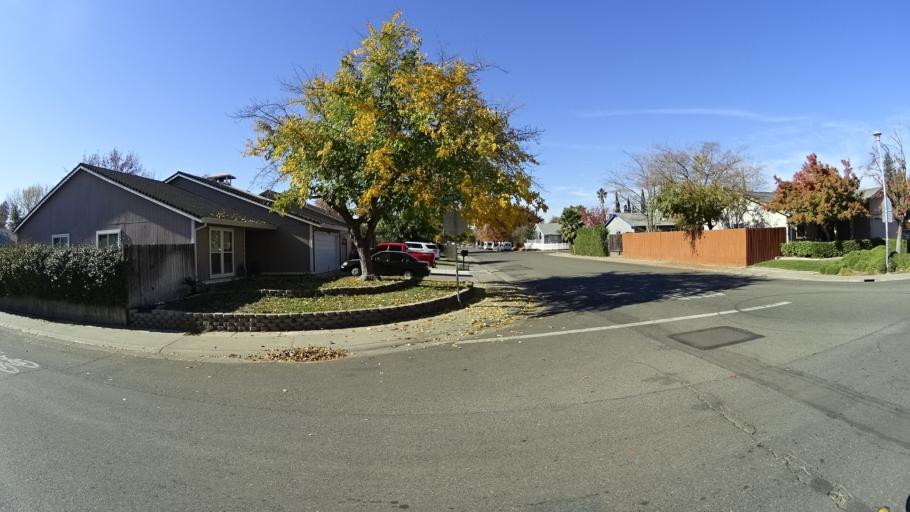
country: US
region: California
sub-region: Sacramento County
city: Antelope
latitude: 38.7198
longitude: -121.3053
